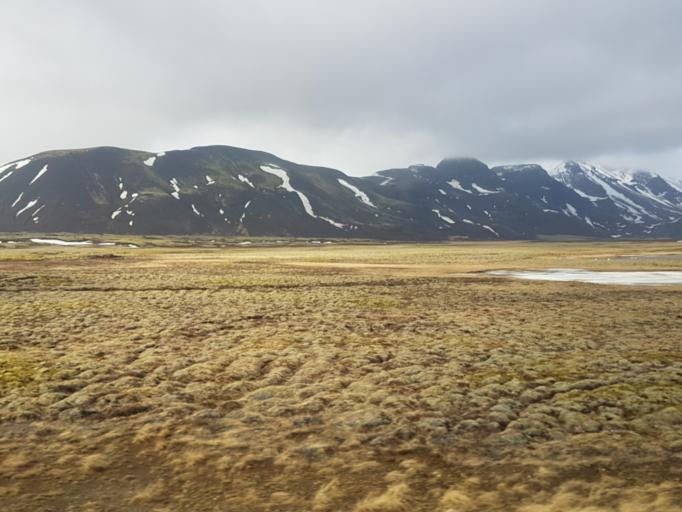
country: IS
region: South
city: Selfoss
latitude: 64.1974
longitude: -20.8836
